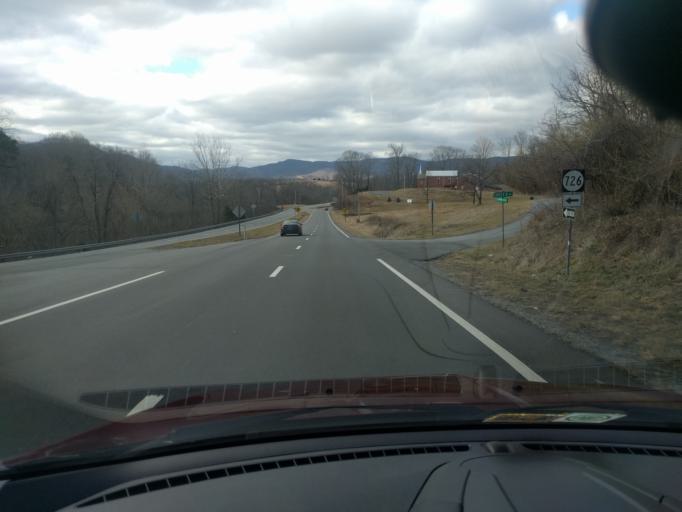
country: US
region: Virginia
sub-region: Botetourt County
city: Blue Ridge
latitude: 37.3688
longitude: -79.6944
